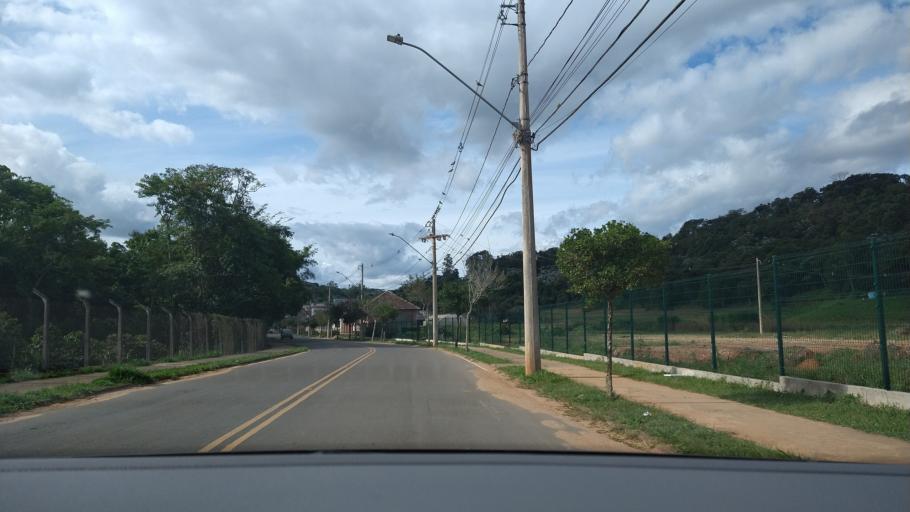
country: BR
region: Minas Gerais
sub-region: Vicosa
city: Vicosa
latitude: -20.7692
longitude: -42.8713
